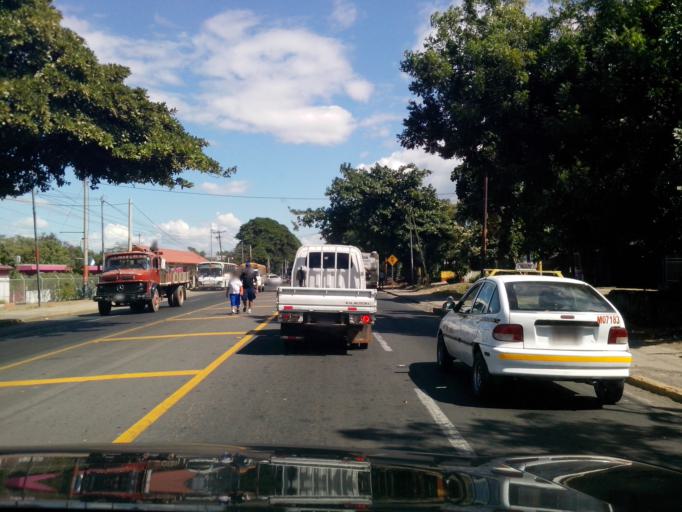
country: NI
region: Managua
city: Ciudad Sandino
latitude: 12.1388
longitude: -86.3007
